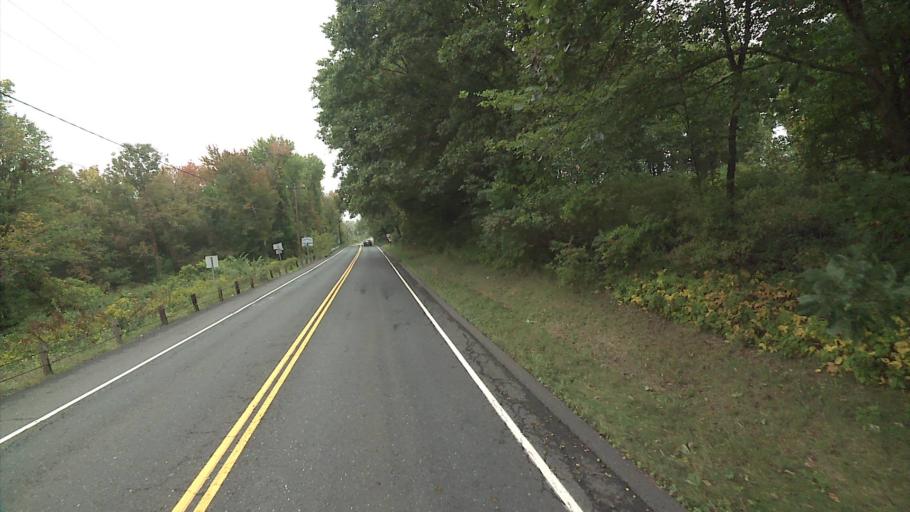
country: US
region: Massachusetts
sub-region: Hampden County
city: Agawam
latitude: 42.0314
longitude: -72.6370
